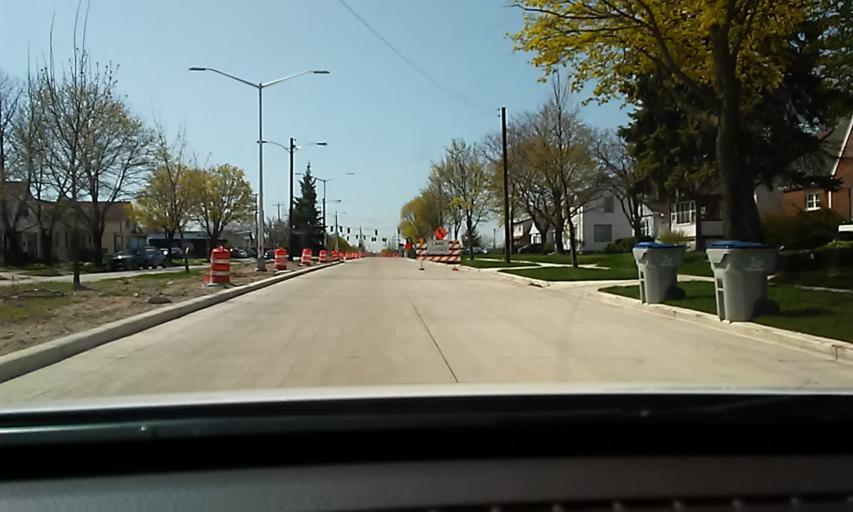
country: US
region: Wisconsin
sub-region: Milwaukee County
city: Greenfield
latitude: 42.9787
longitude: -87.9880
